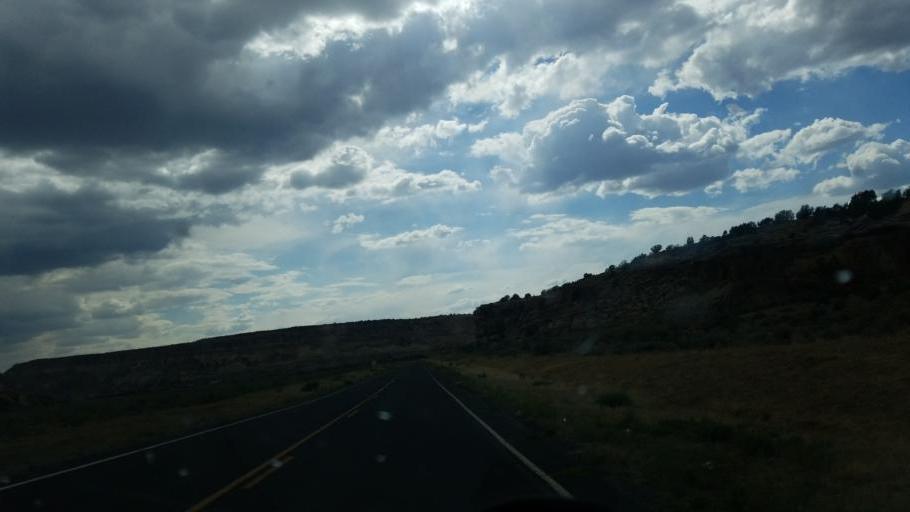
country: US
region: Arizona
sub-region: Apache County
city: Saint Michaels
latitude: 35.4155
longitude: -108.9844
